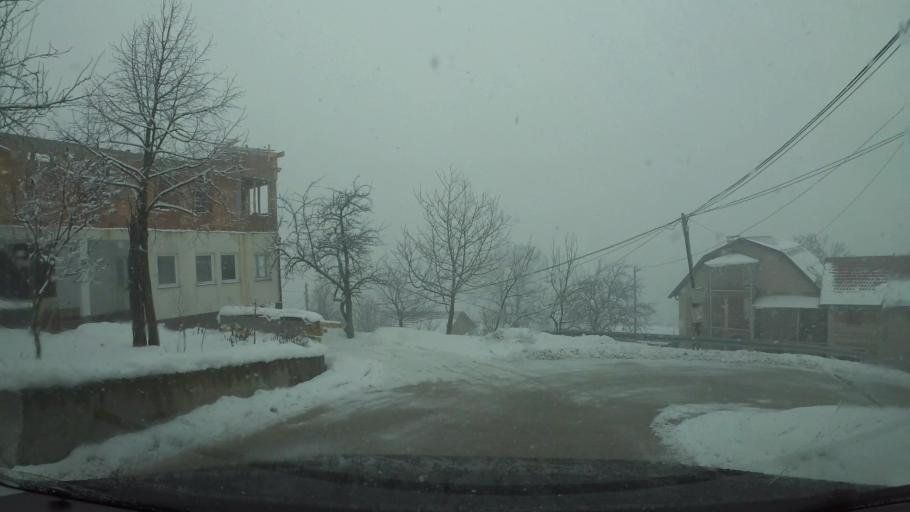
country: BA
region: Federation of Bosnia and Herzegovina
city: Kobilja Glava
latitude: 43.8507
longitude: 18.4434
